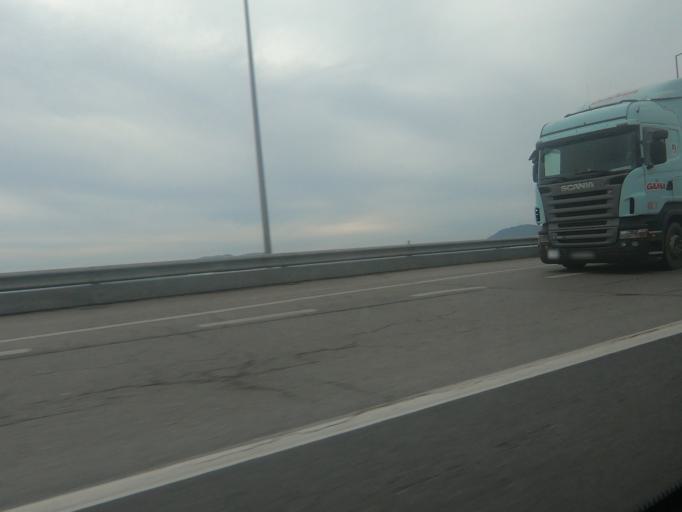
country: PT
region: Setubal
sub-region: Setubal
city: Setubal
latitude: 38.5037
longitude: -8.8437
